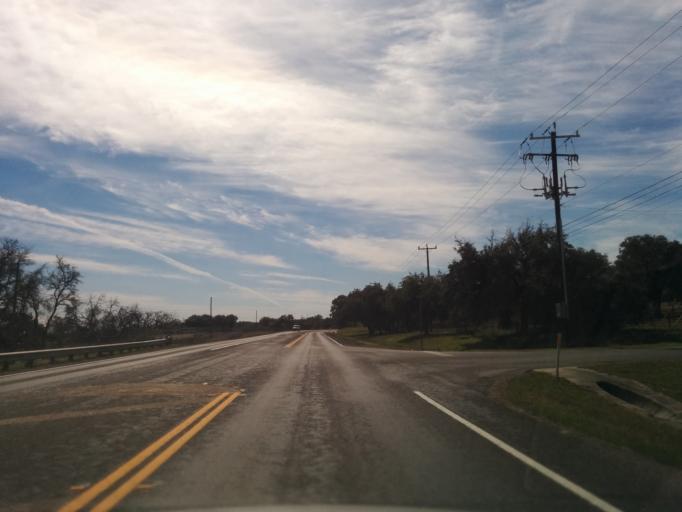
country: US
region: Texas
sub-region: Bexar County
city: Fair Oaks Ranch
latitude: 29.7207
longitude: -98.6237
